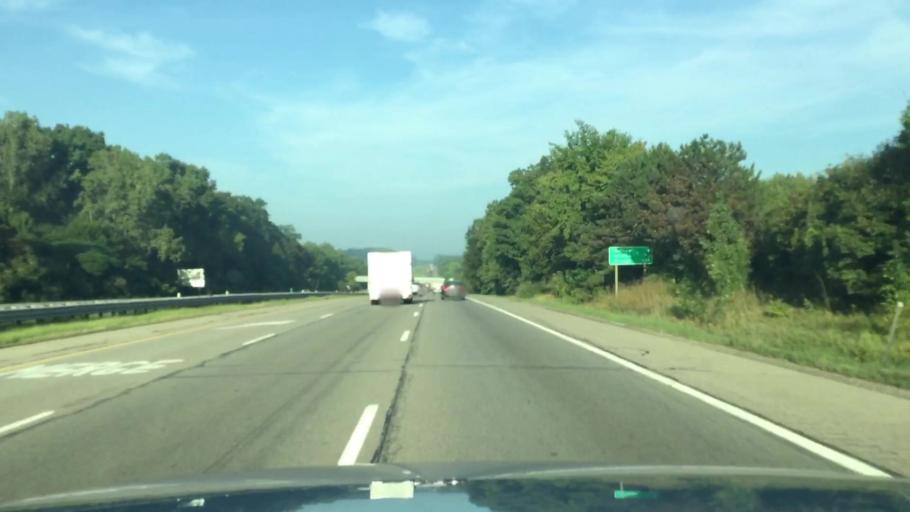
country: US
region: Michigan
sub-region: Washtenaw County
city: Dexter
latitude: 42.2982
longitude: -83.8916
